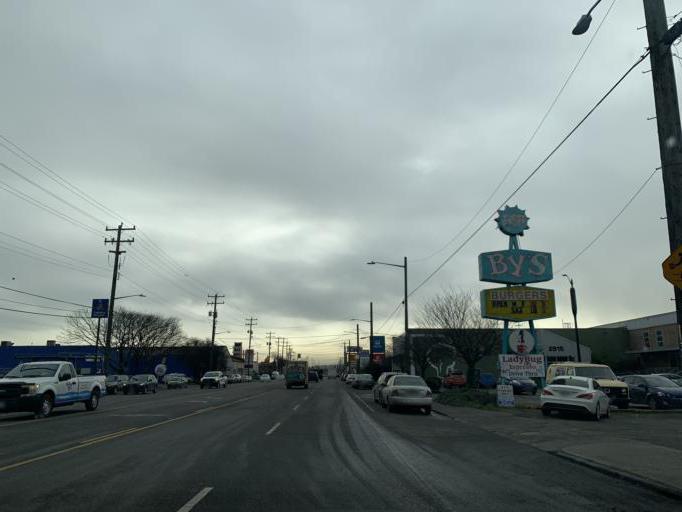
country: US
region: Washington
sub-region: King County
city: Seattle
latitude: 47.5776
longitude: -122.3292
